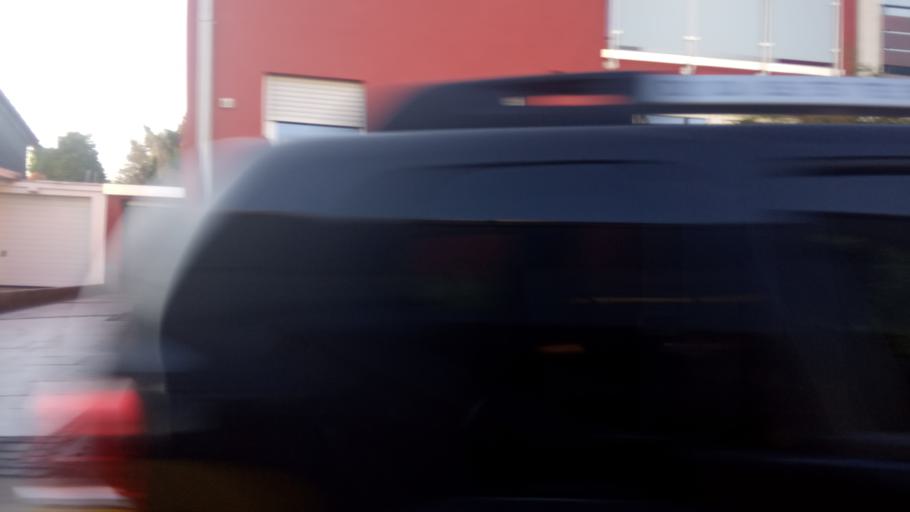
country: DE
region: North Rhine-Westphalia
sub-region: Regierungsbezirk Dusseldorf
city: Velbert
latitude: 51.3911
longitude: 7.0166
